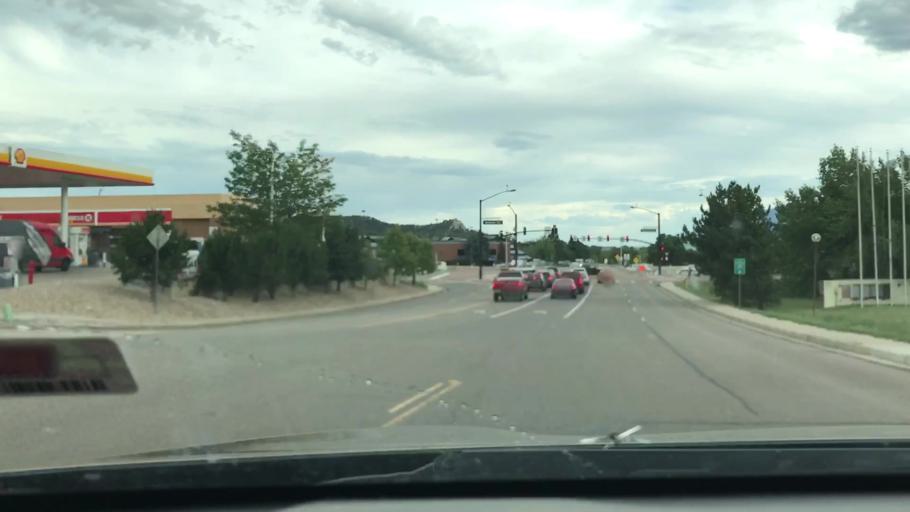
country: US
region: Colorado
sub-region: El Paso County
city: Air Force Academy
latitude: 38.9340
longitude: -104.8152
